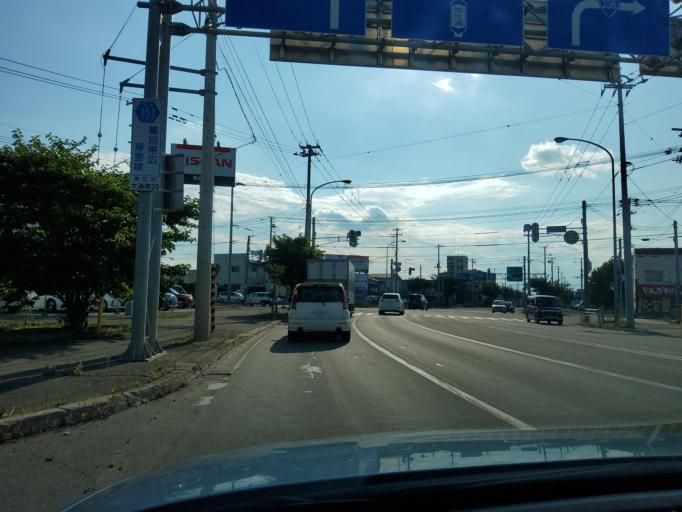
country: JP
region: Hokkaido
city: Obihiro
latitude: 42.8996
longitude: 143.2090
